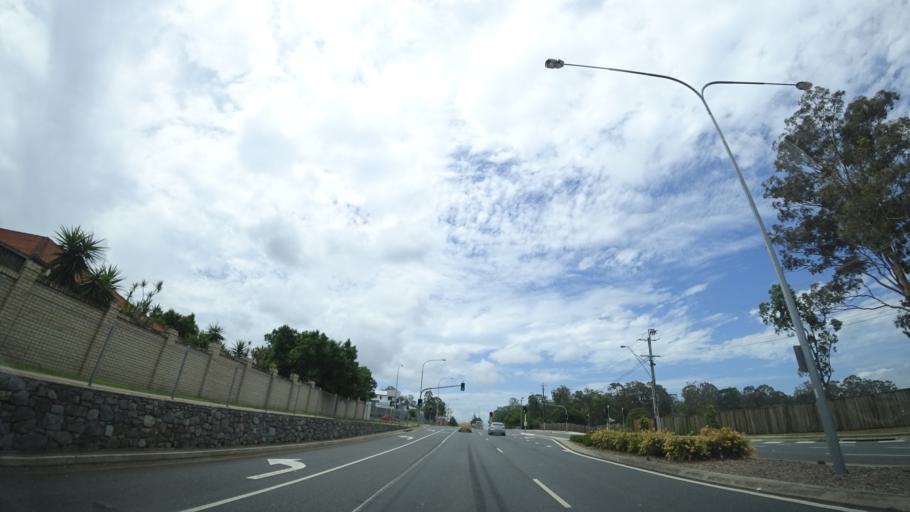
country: AU
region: Queensland
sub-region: Brisbane
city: Bridegman Downs
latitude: -27.3612
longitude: 152.9922
